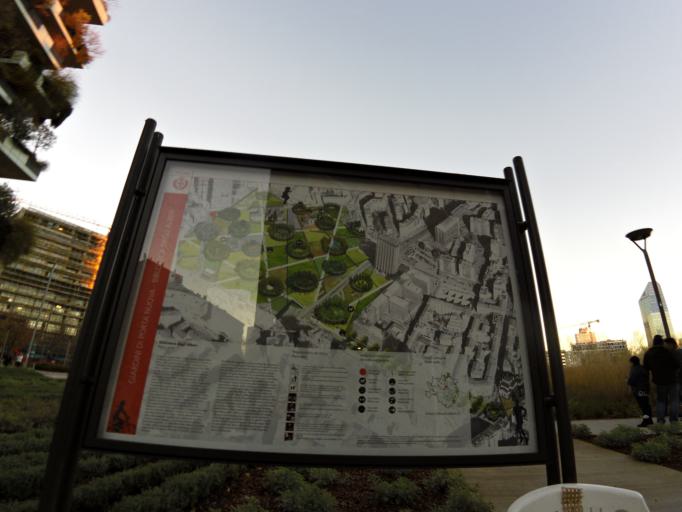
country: IT
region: Lombardy
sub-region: Citta metropolitana di Milano
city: Milano
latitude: 45.4854
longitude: 9.1904
